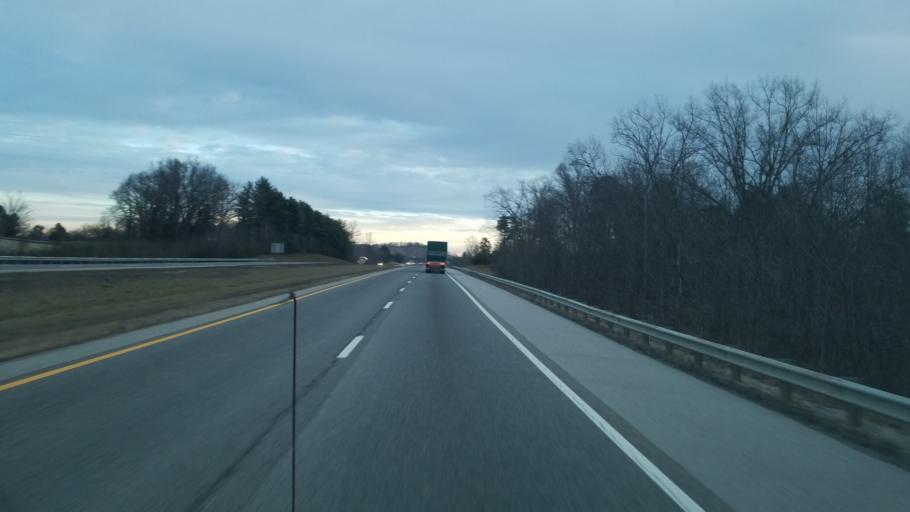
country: US
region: Tennessee
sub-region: Putnam County
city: Cookeville
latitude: 36.1175
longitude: -85.4925
